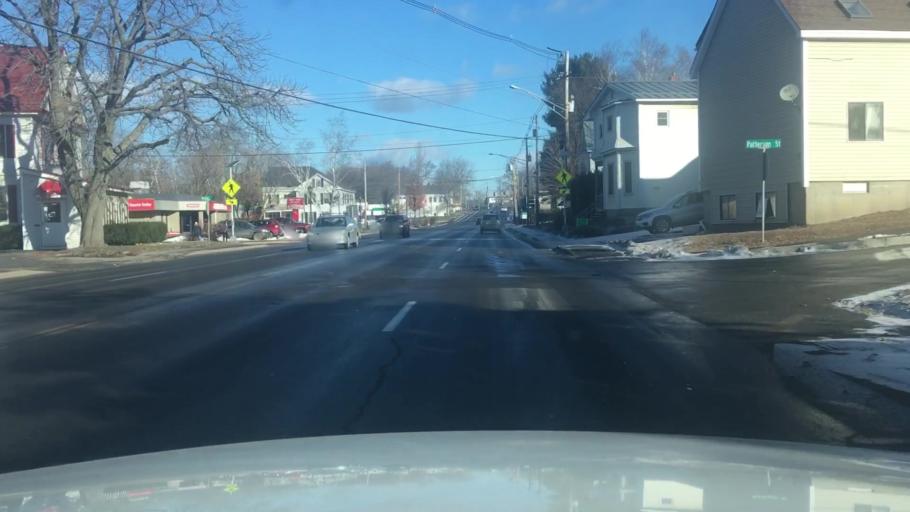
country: US
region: Maine
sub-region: Kennebec County
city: Augusta
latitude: 44.3182
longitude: -69.7668
